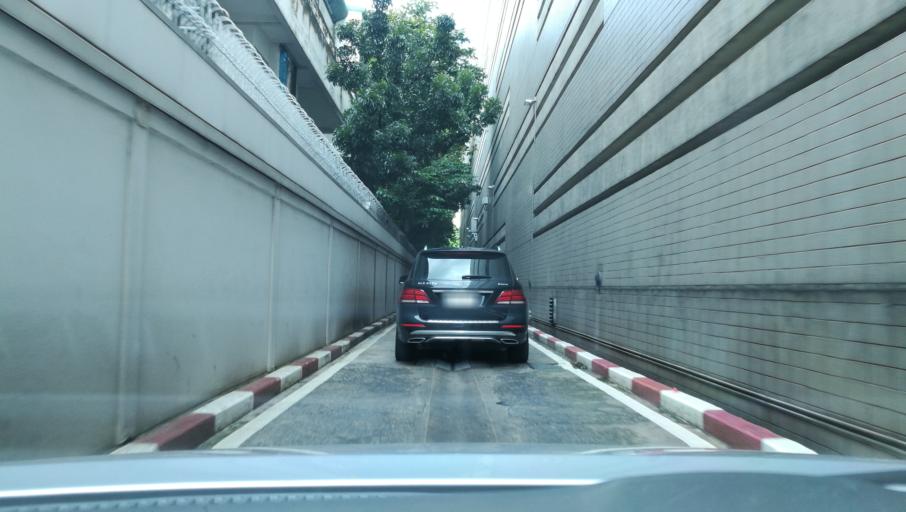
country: TH
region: Bangkok
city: Ratchathewi
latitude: 13.7469
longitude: 100.5325
